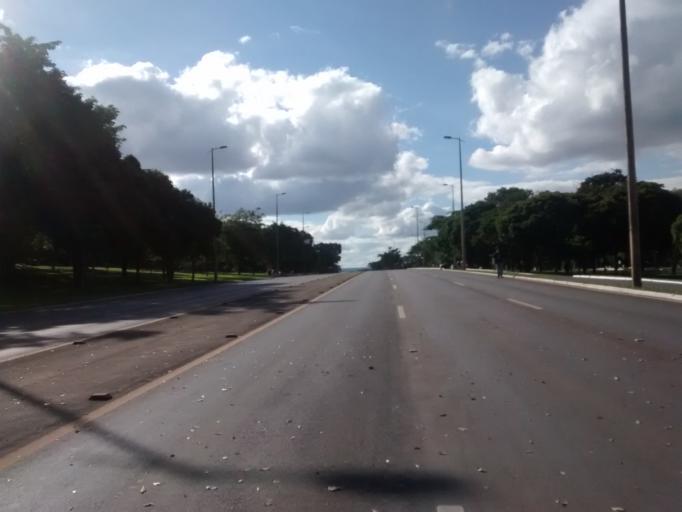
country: BR
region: Federal District
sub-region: Brasilia
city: Brasilia
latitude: -15.7734
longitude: -47.8813
